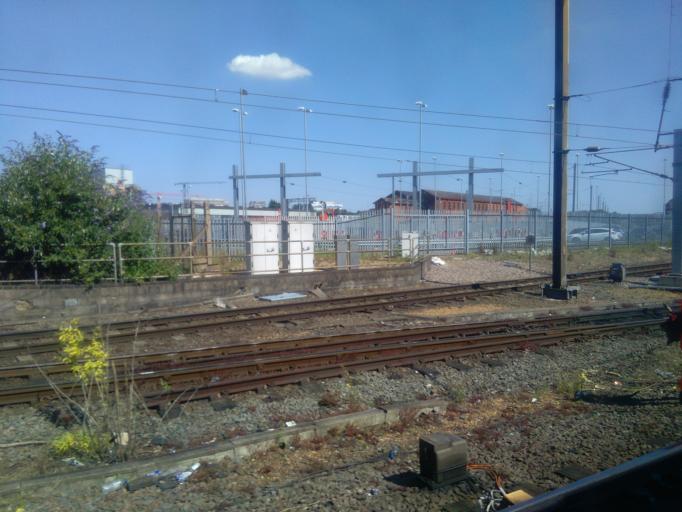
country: GB
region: England
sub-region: Bedford
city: Bedford
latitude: 52.1341
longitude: -0.4781
